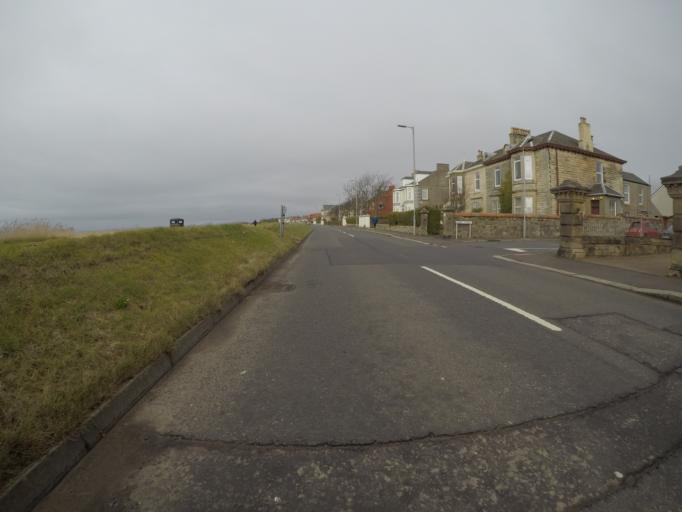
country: GB
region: Scotland
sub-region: North Ayrshire
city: Ardrossan
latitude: 55.6482
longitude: -4.8138
